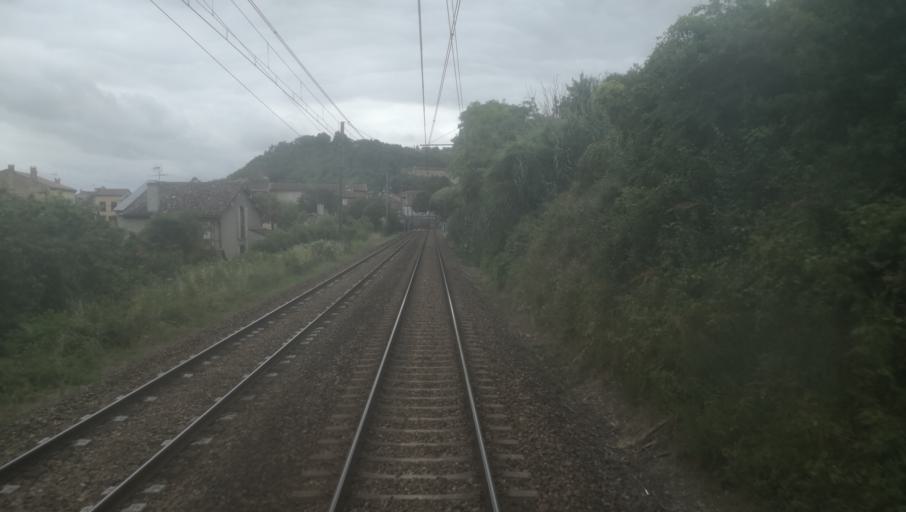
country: FR
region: Midi-Pyrenees
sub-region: Departement du Tarn-et-Garonne
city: Moissac
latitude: 44.1065
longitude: 1.0898
